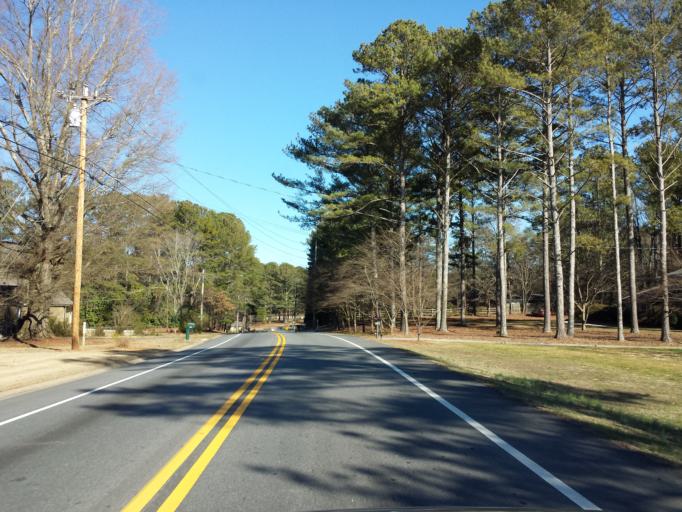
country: US
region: Georgia
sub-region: Cobb County
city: Kennesaw
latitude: 33.9668
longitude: -84.6292
